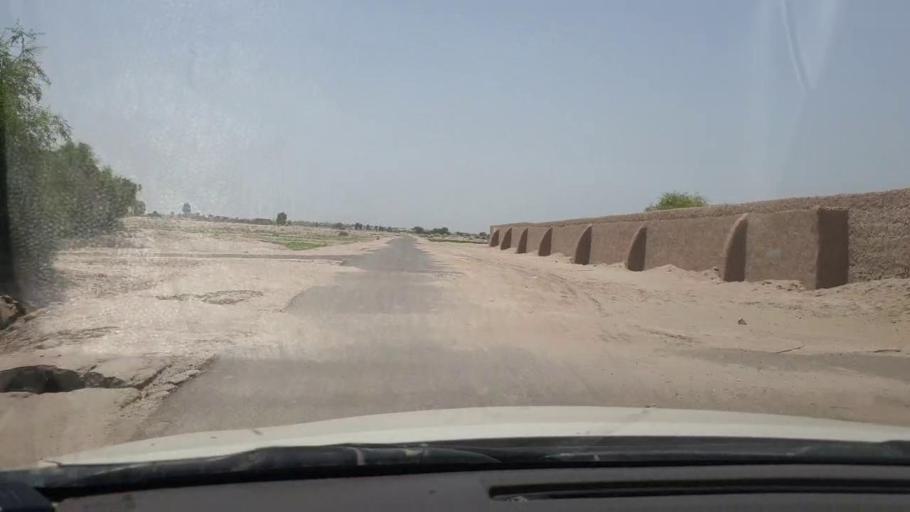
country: PK
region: Sindh
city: Rohri
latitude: 27.5207
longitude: 69.1655
